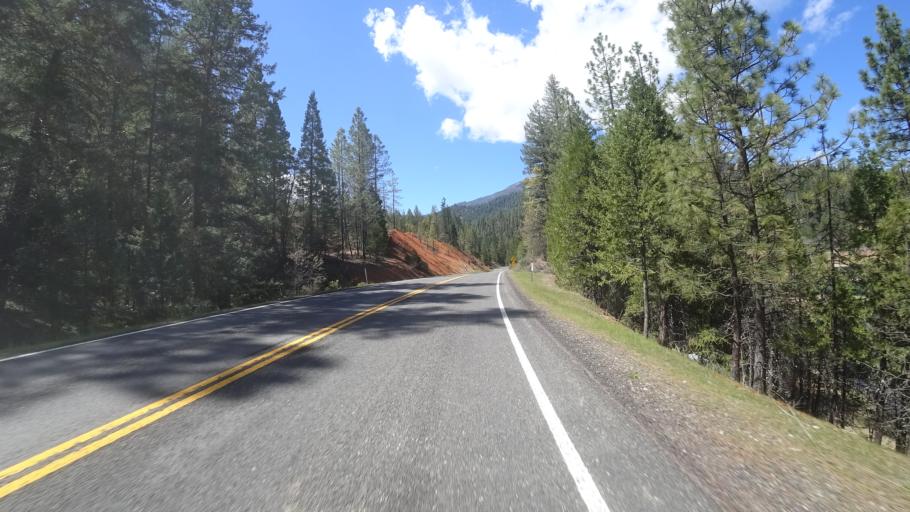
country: US
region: California
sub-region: Trinity County
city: Weaverville
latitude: 40.8479
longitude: -122.8655
